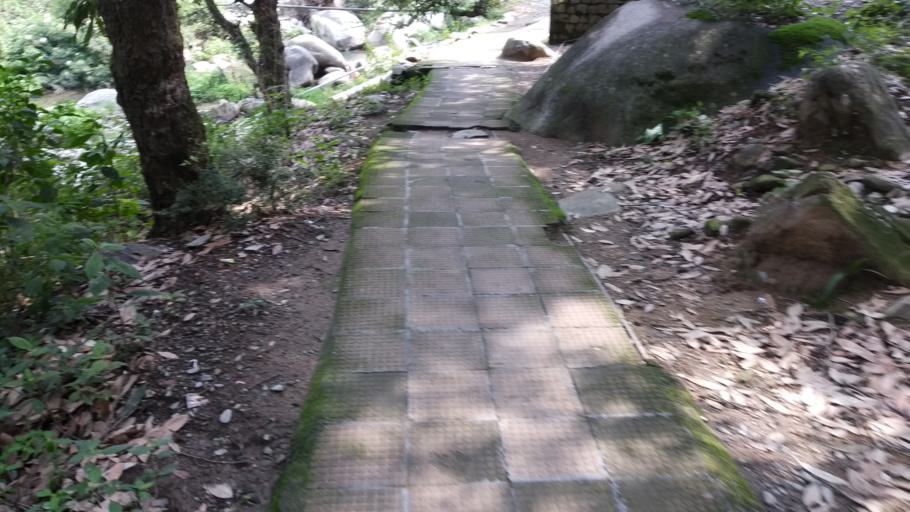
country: IN
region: Himachal Pradesh
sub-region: Kangra
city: Dharmsala
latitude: 32.1734
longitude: 76.3889
